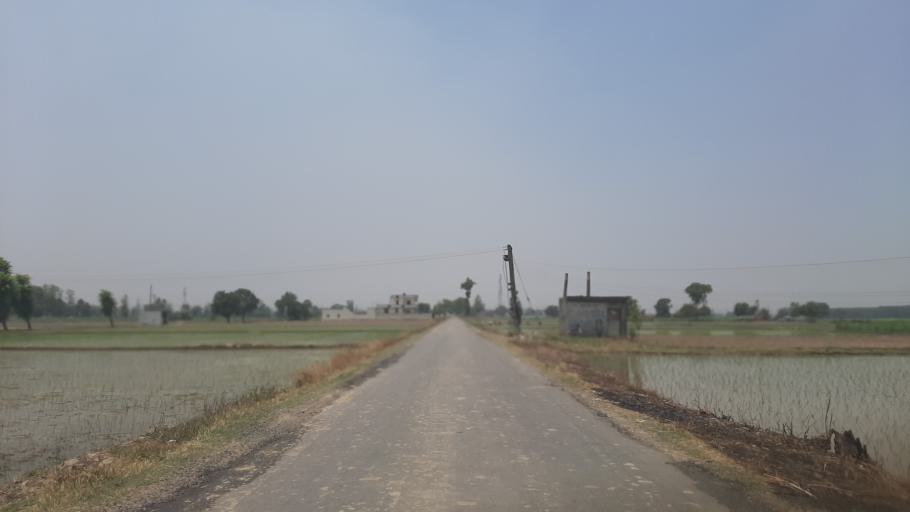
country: IN
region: Haryana
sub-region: Yamunanagar
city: Yamunanagar
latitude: 30.1651
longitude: 77.2395
